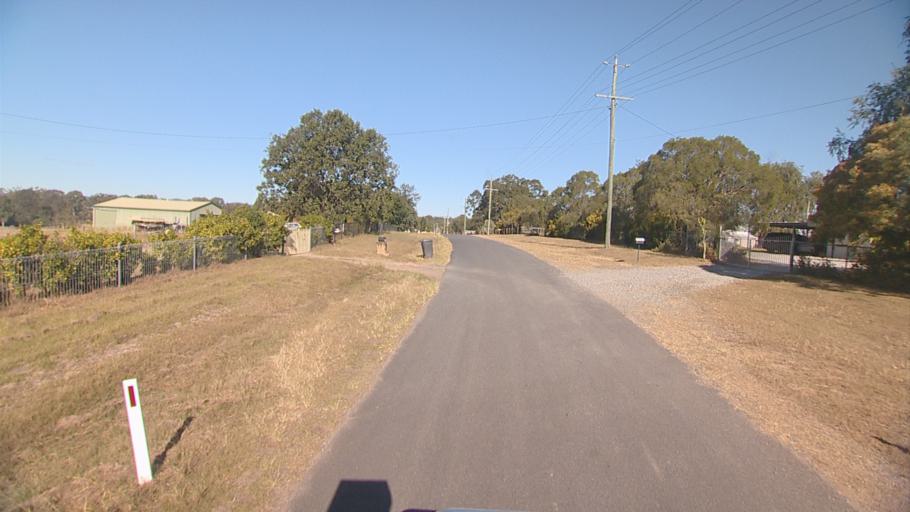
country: AU
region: Queensland
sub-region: Logan
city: North Maclean
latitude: -27.7828
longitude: 153.0189
